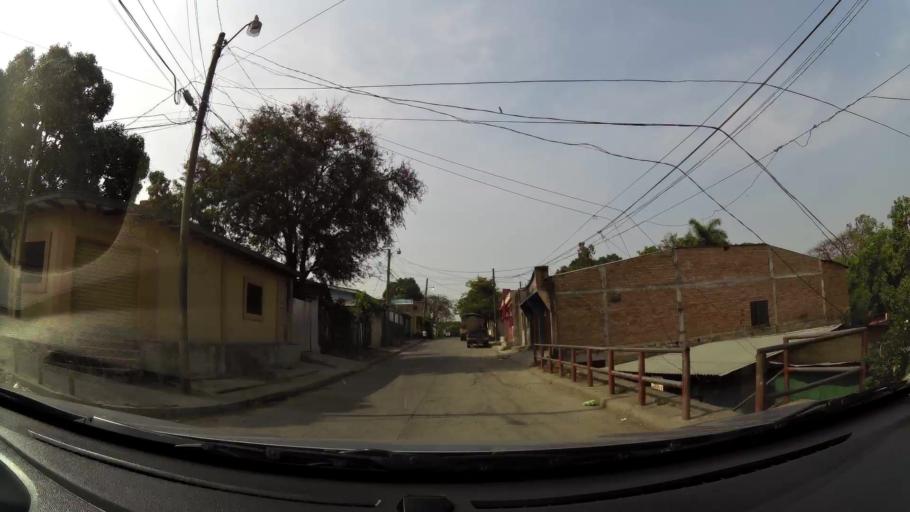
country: HN
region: Comayagua
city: Comayagua
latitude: 14.4527
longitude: -87.6411
